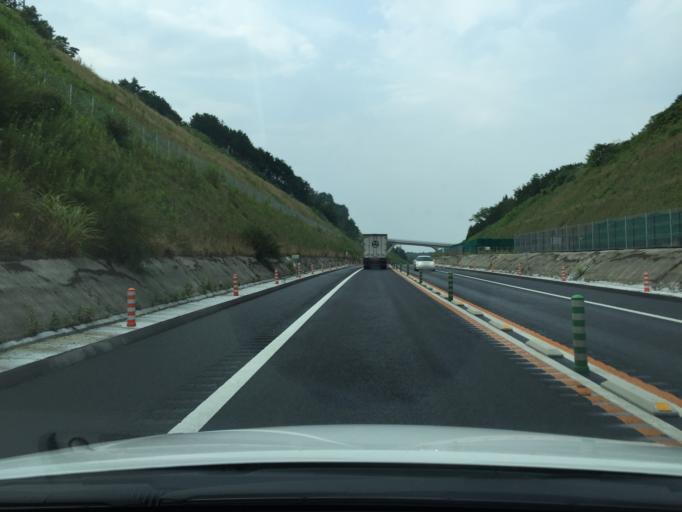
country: JP
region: Fukushima
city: Namie
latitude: 37.4376
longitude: 140.9582
